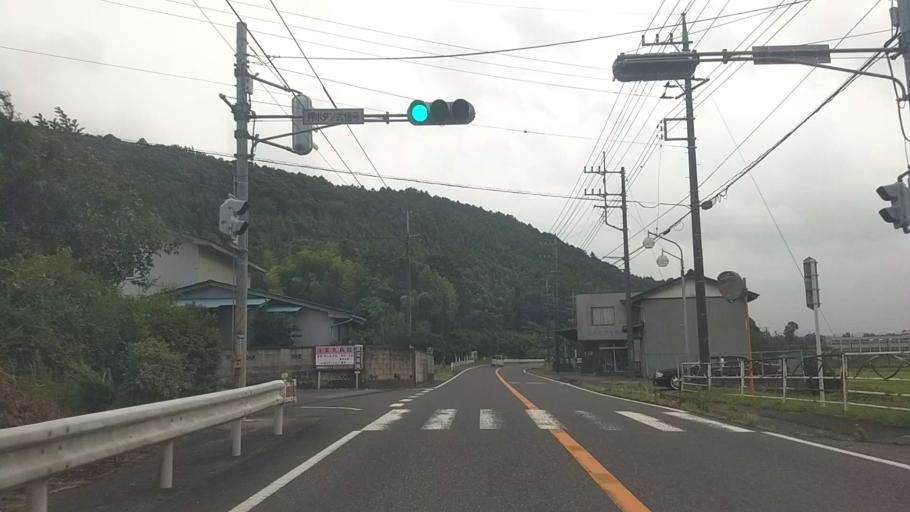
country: JP
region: Chiba
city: Kisarazu
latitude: 35.3055
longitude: 140.0704
